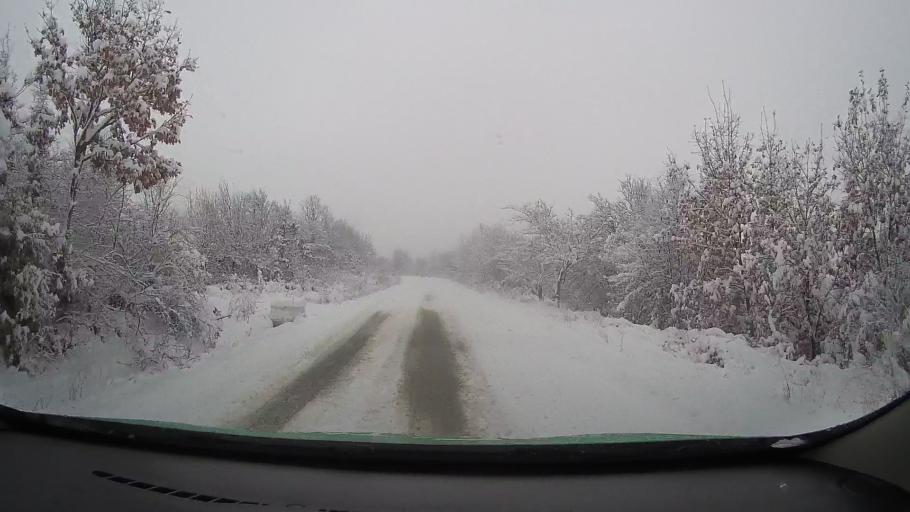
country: RO
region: Hunedoara
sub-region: Comuna Teliucu Inferior
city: Teliucu Inferior
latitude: 45.6965
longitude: 22.8921
